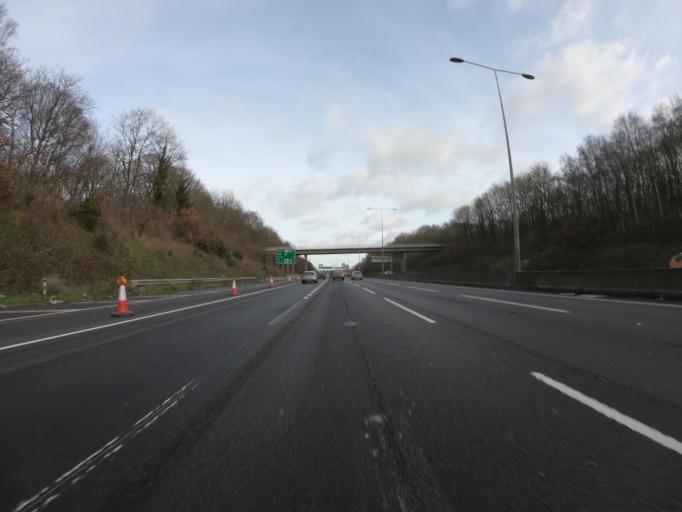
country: GB
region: England
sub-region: Kent
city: Stone
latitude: 51.4299
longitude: 0.2689
